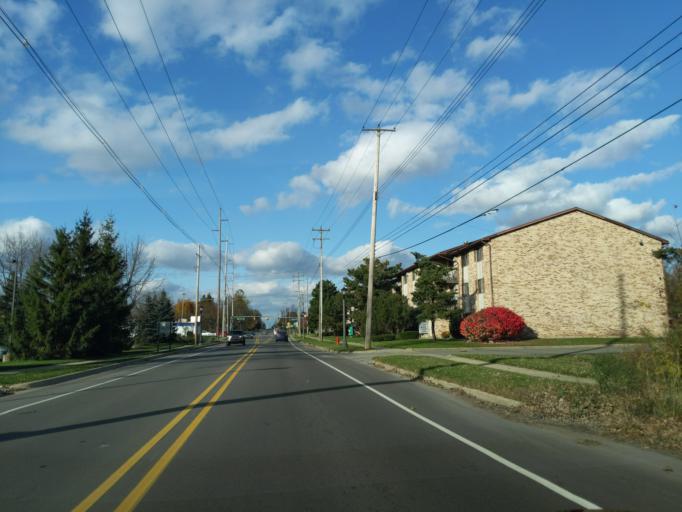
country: US
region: Michigan
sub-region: Ingham County
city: Lansing
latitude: 42.7589
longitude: -84.5231
